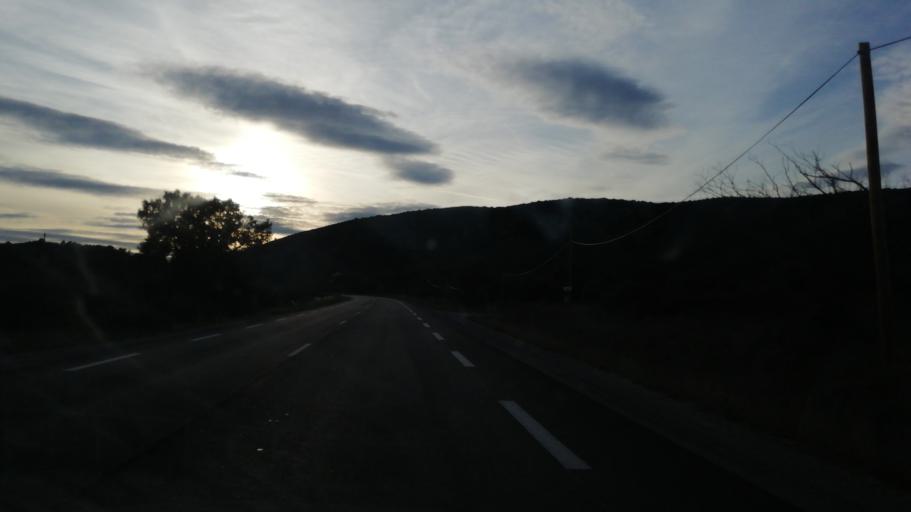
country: FR
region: Languedoc-Roussillon
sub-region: Departement du Gard
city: Quissac
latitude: 43.8997
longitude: 3.9881
